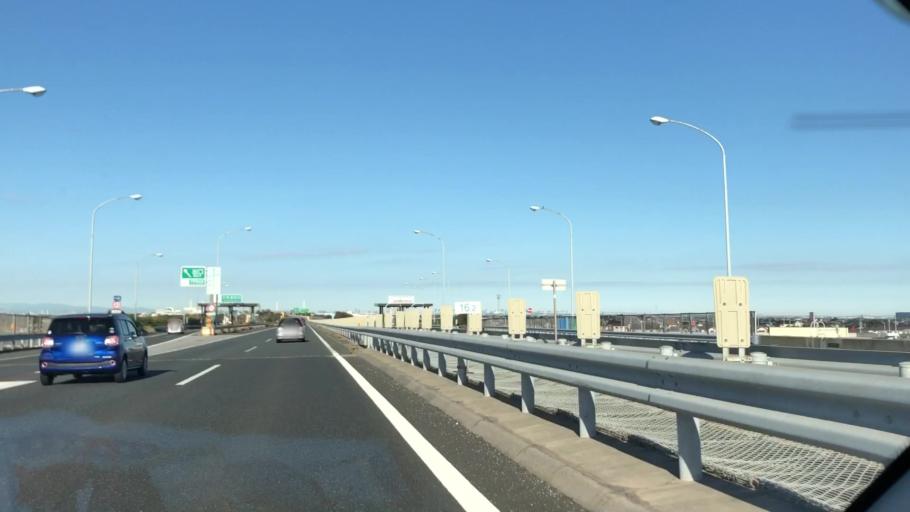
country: JP
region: Chiba
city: Kisarazu
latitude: 35.4268
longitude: 139.9298
